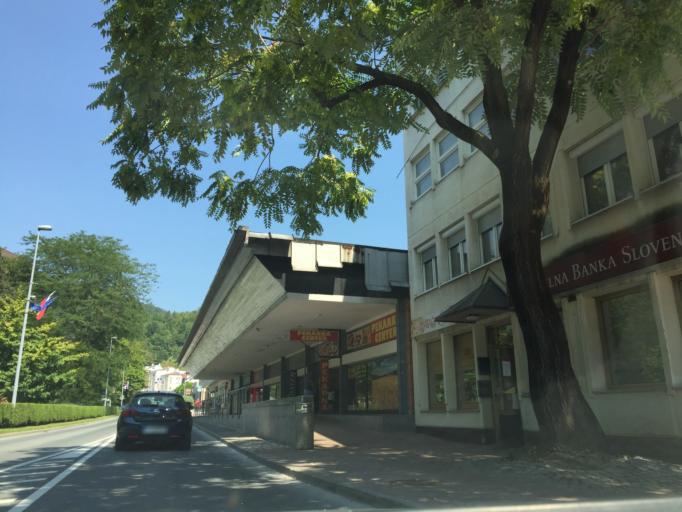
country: SI
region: Zagorje ob Savi
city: Zagorje ob Savi
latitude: 46.1318
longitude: 14.9959
